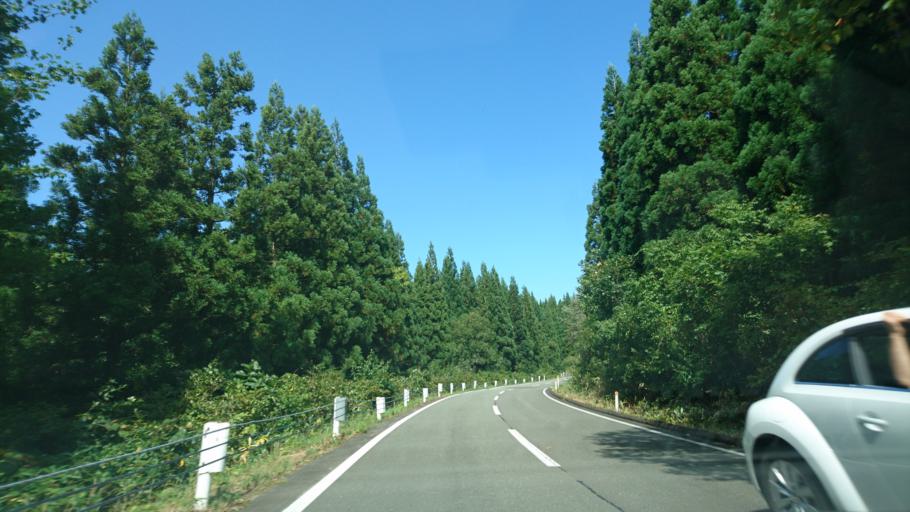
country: JP
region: Akita
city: Yuzawa
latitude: 38.9735
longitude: 140.7101
